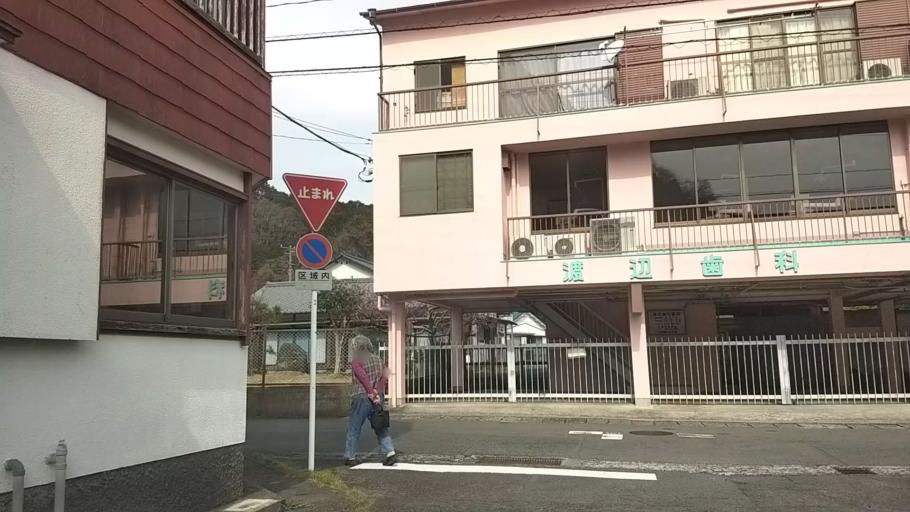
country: JP
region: Shizuoka
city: Shimoda
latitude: 34.6847
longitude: 138.9421
